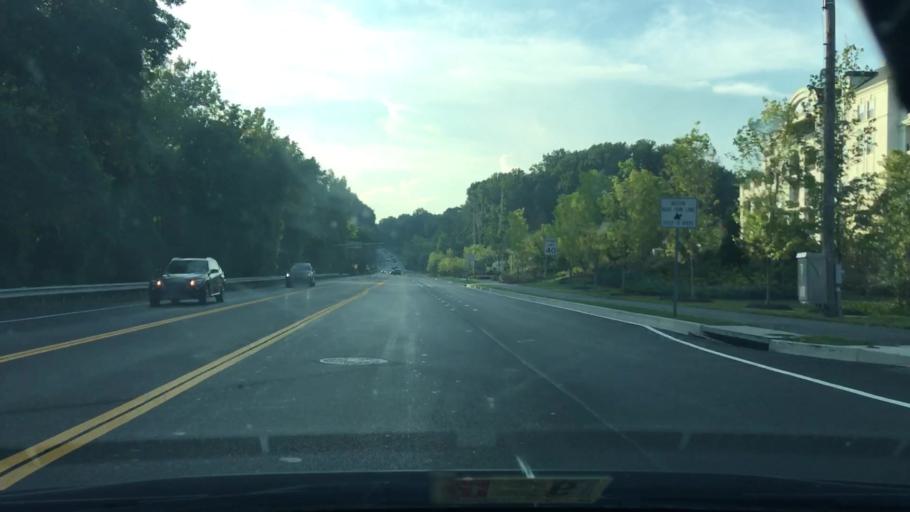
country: US
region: Maryland
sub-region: Montgomery County
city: Cabin John
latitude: 38.9943
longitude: -77.1646
